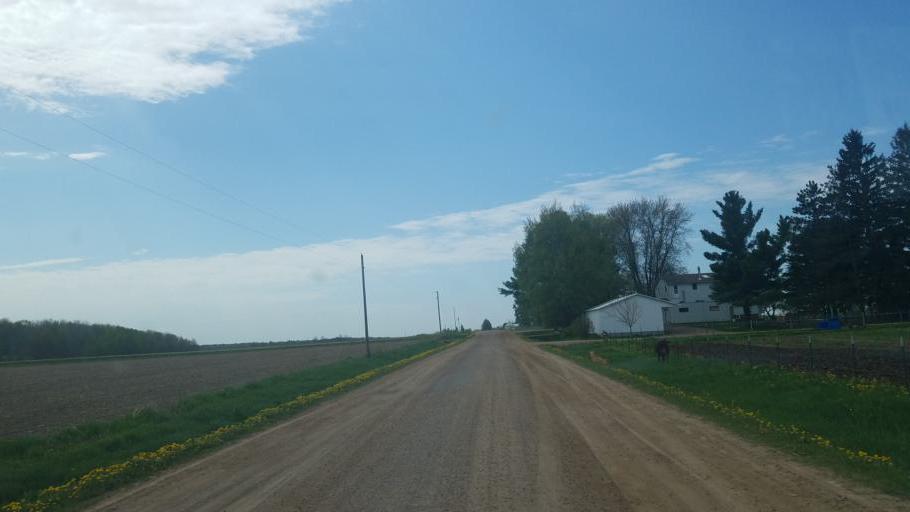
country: US
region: Wisconsin
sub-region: Marathon County
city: Spencer
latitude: 44.6421
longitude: -90.3774
